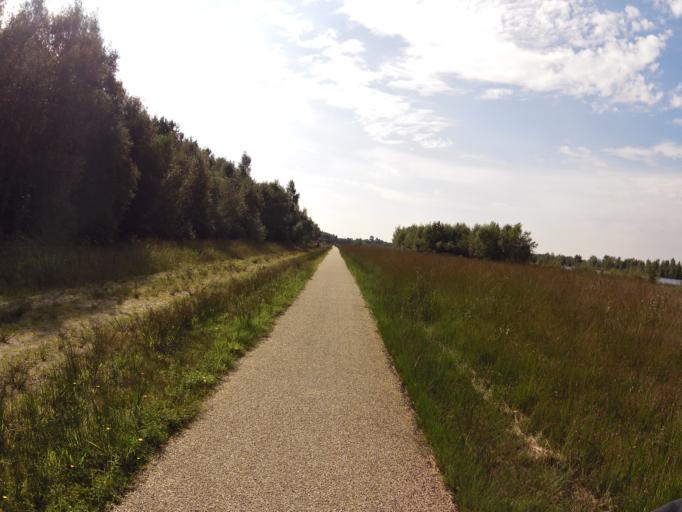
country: DE
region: Lower Saxony
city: Twist
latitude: 52.6661
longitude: 7.0572
